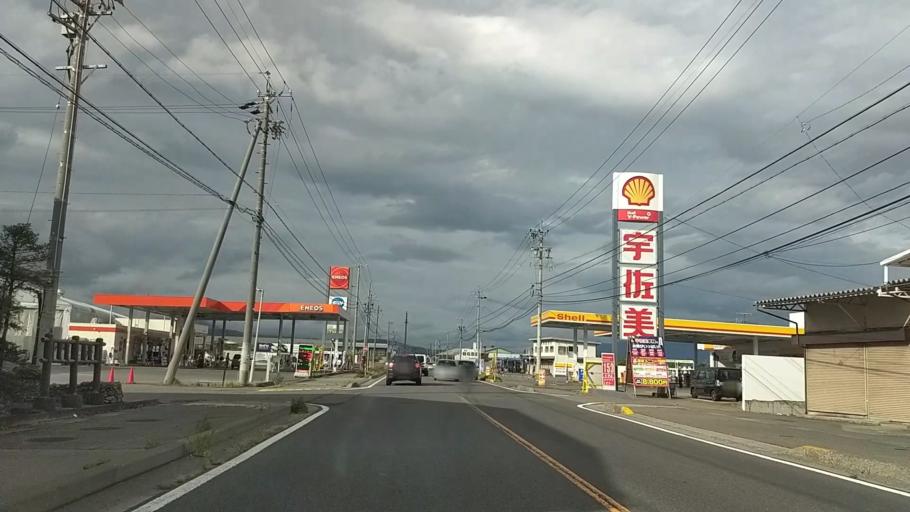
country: JP
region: Nagano
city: Suzaka
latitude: 36.6718
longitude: 138.2657
